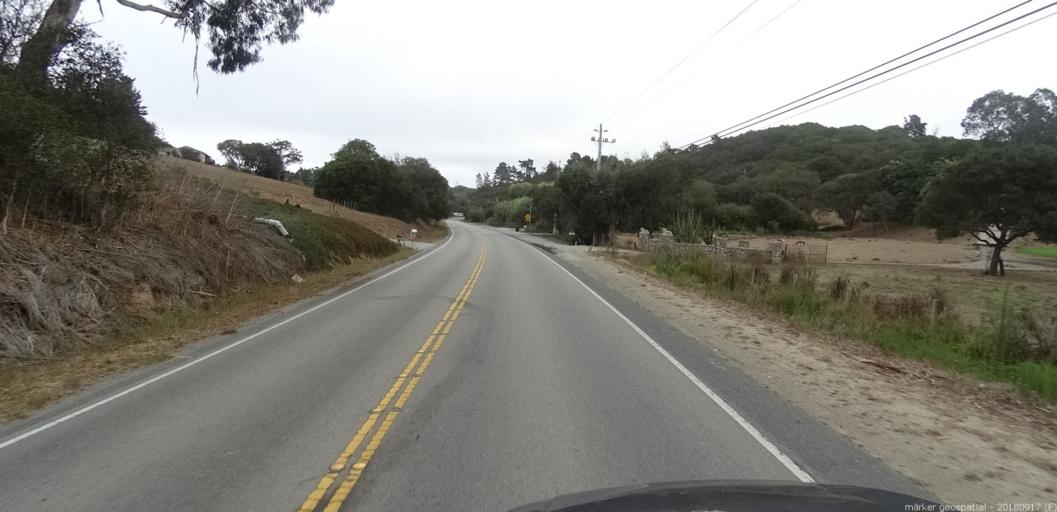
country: US
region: California
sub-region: Monterey County
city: Prunedale
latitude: 36.7971
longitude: -121.7012
